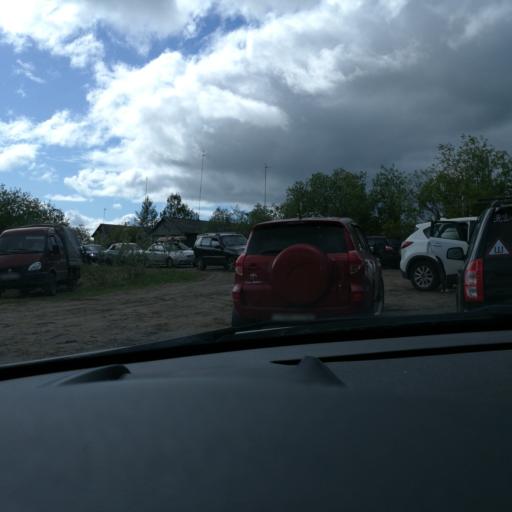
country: RU
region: Arkhangelskaya
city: Kholmogory
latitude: 64.2349
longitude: 41.6389
